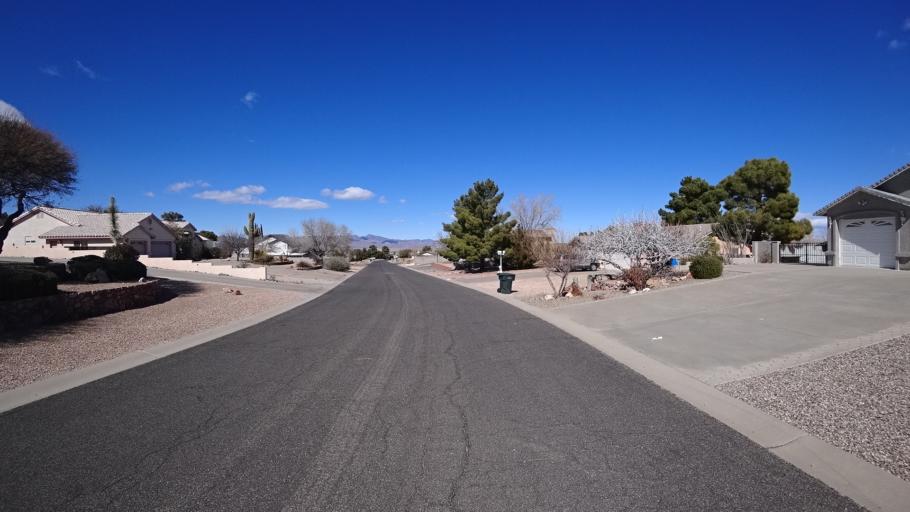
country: US
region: Arizona
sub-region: Mohave County
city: Kingman
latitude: 35.1994
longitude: -113.9661
